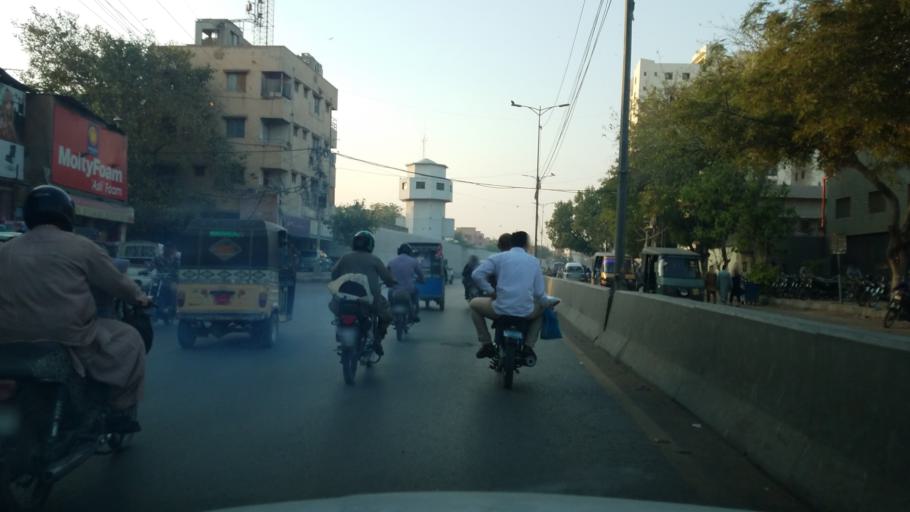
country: PK
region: Sindh
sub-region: Karachi District
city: Karachi
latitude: 24.8679
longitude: 67.0233
